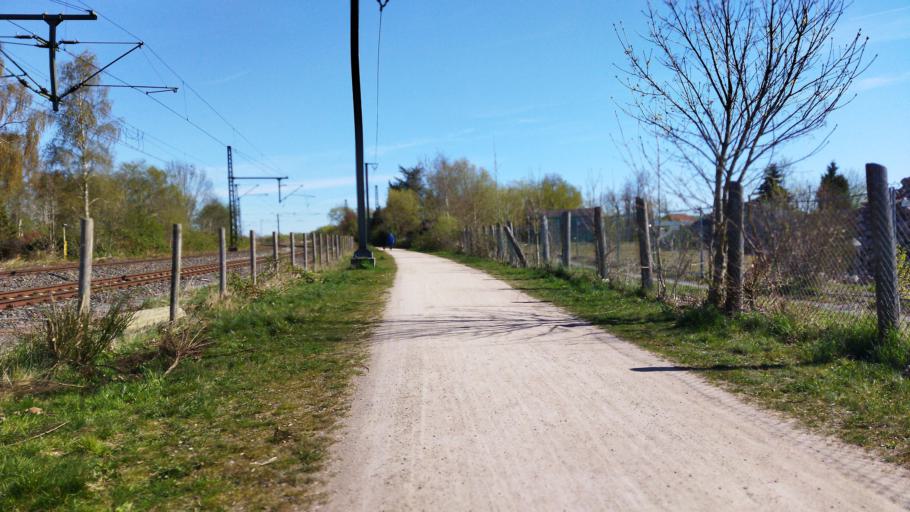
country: DE
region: Lower Saxony
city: Elsfleth
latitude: 53.2305
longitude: 8.4617
